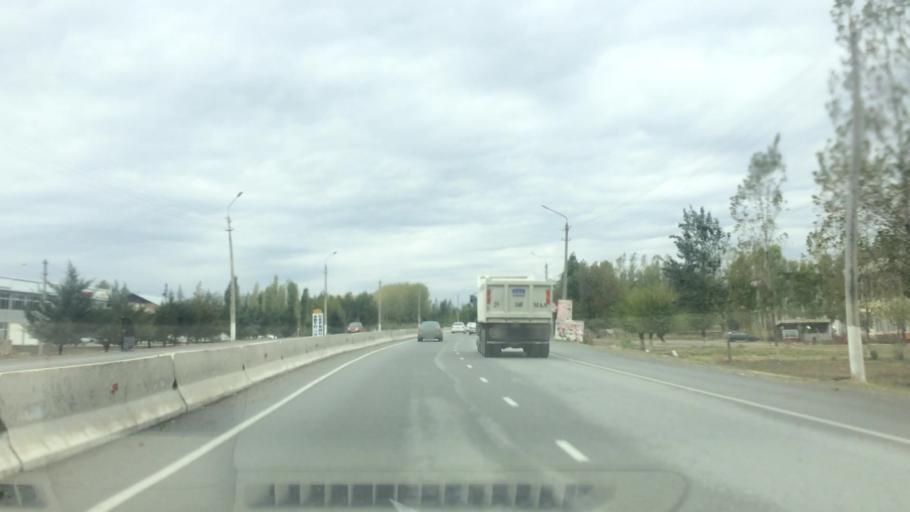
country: UZ
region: Jizzax
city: Jizzax
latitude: 39.9916
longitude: 67.5838
